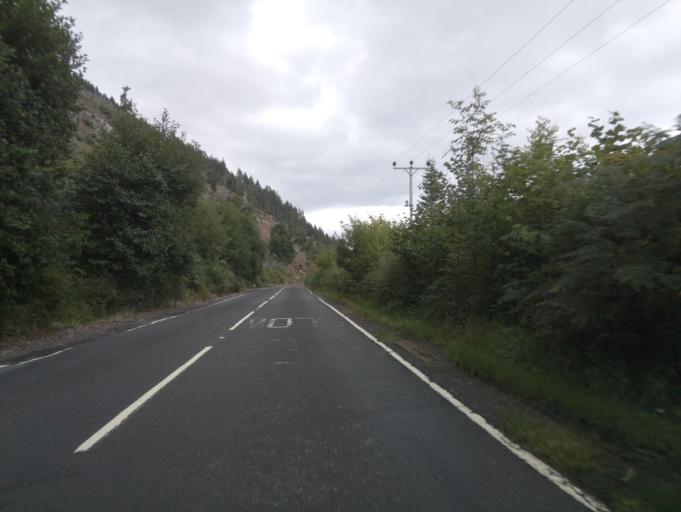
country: GB
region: Scotland
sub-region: Highland
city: Beauly
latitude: 57.2508
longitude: -4.5347
